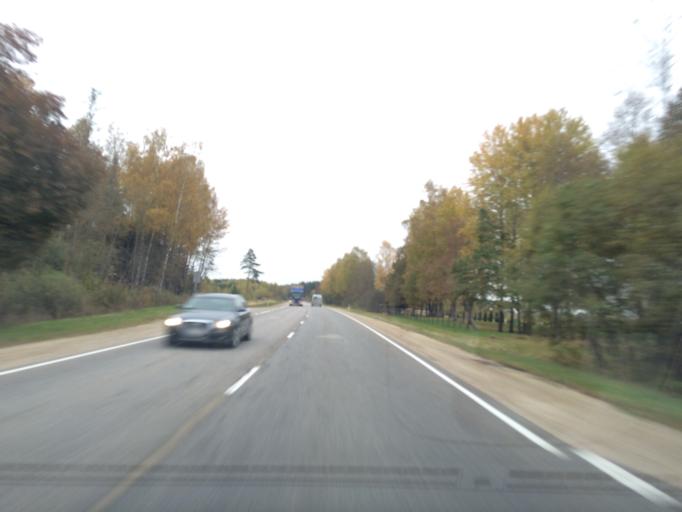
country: LV
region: Koknese
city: Koknese
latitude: 56.5911
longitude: 25.5541
